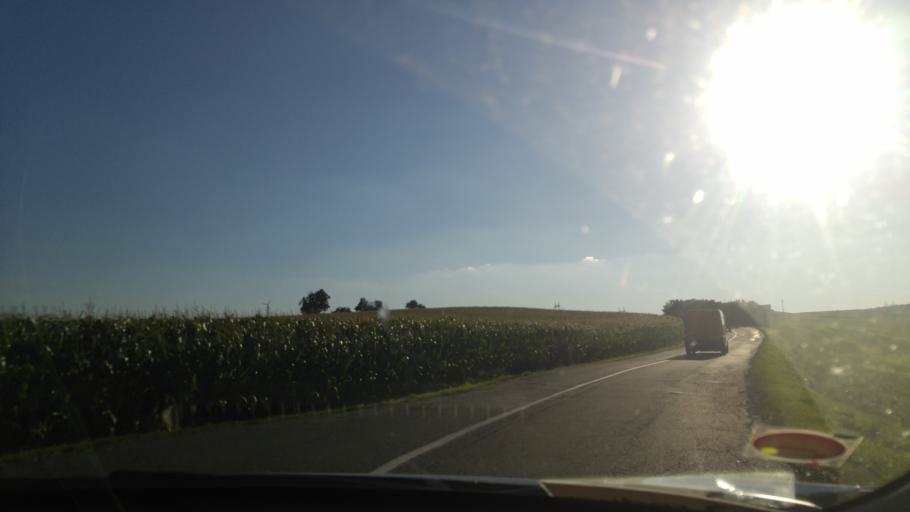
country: CZ
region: South Moravian
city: Ricany
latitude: 49.2219
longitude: 16.4160
